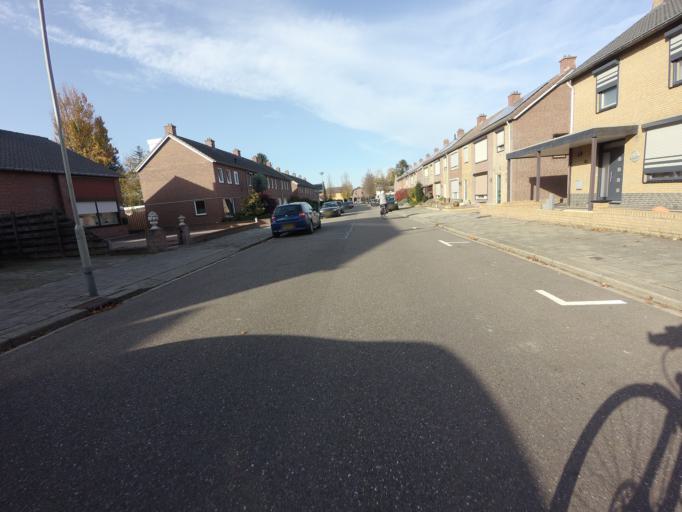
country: NL
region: Limburg
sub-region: Gemeente Echt-Susteren
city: Koningsbosch
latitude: 51.0515
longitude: 5.9531
